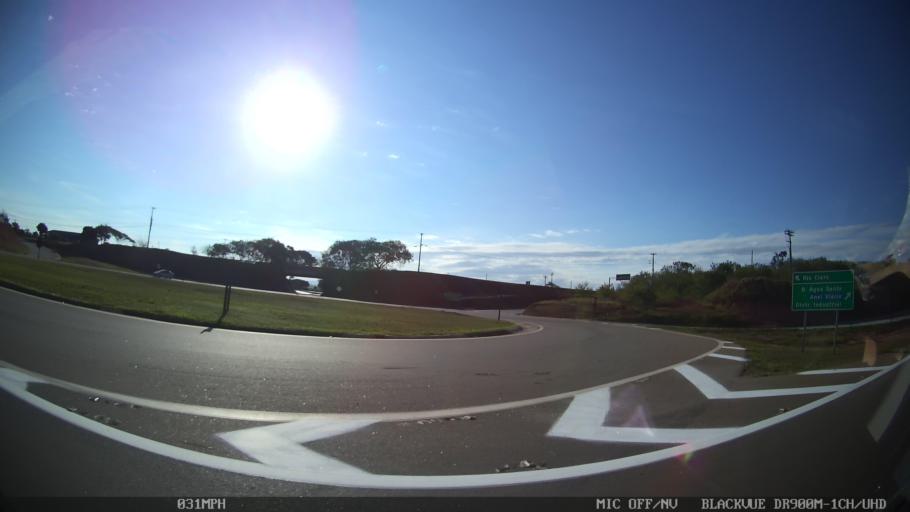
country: BR
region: Sao Paulo
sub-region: Piracicaba
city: Piracicaba
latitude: -22.6648
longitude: -47.6170
